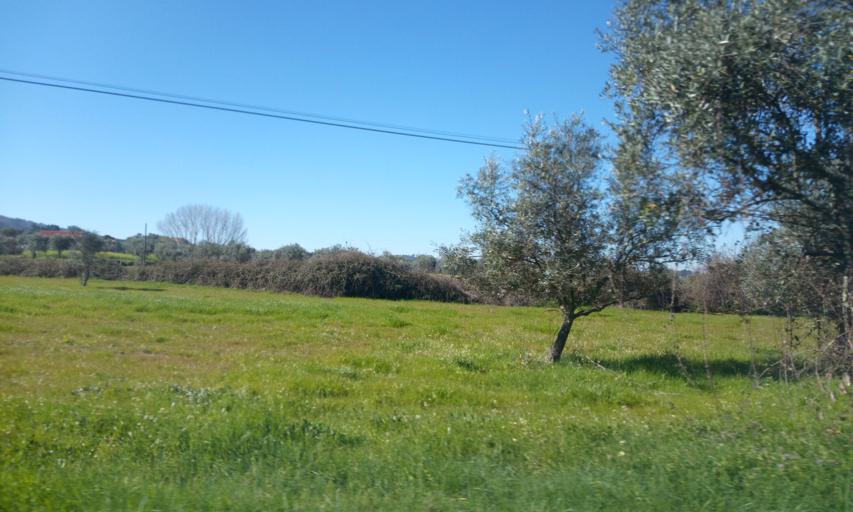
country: PT
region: Guarda
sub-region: Fornos de Algodres
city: Fornos de Algodres
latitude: 40.5284
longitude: -7.5571
